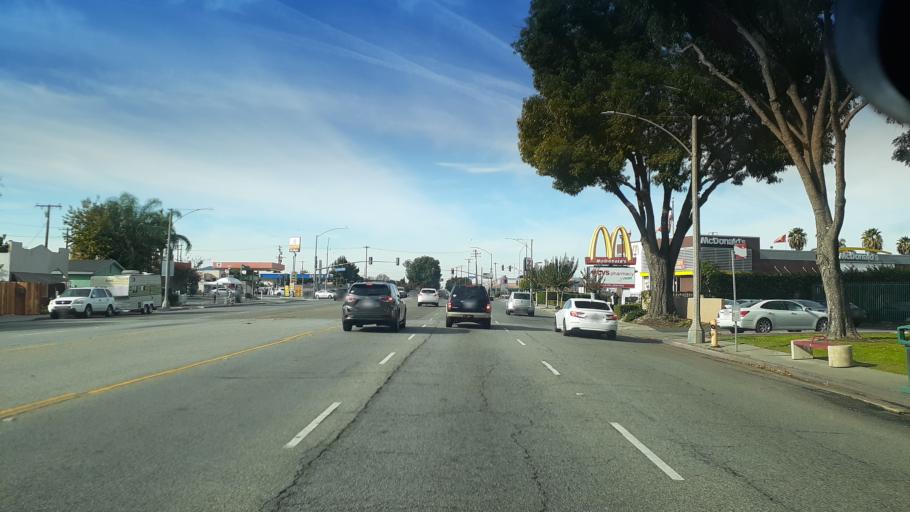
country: US
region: California
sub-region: Los Angeles County
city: Signal Hill
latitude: 33.8468
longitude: -118.1923
